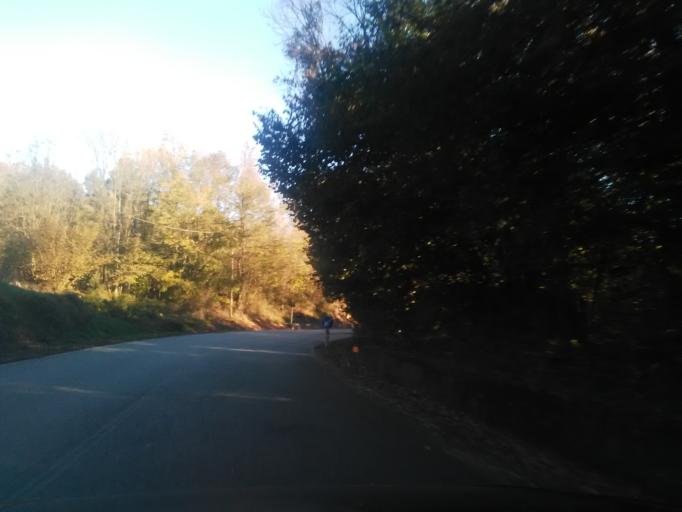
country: IT
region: Piedmont
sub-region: Provincia di Biella
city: Sostegno
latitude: 45.6385
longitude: 8.2718
